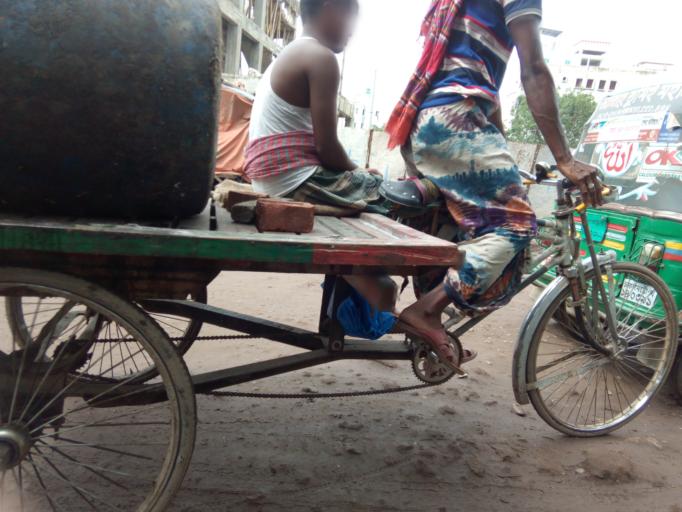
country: BD
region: Dhaka
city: Azimpur
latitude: 23.7246
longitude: 90.3706
